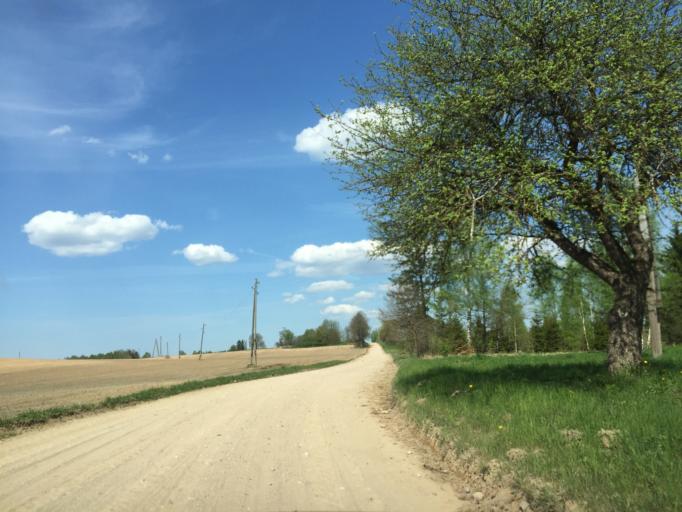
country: LV
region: Krimulda
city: Ragana
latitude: 57.3451
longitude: 24.6526
